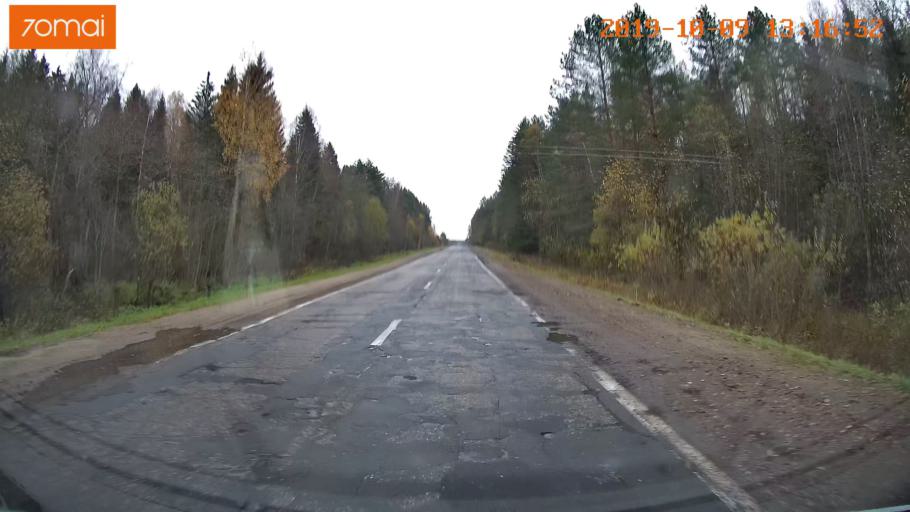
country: RU
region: Jaroslavl
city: Lyubim
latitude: 58.3580
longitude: 40.7719
